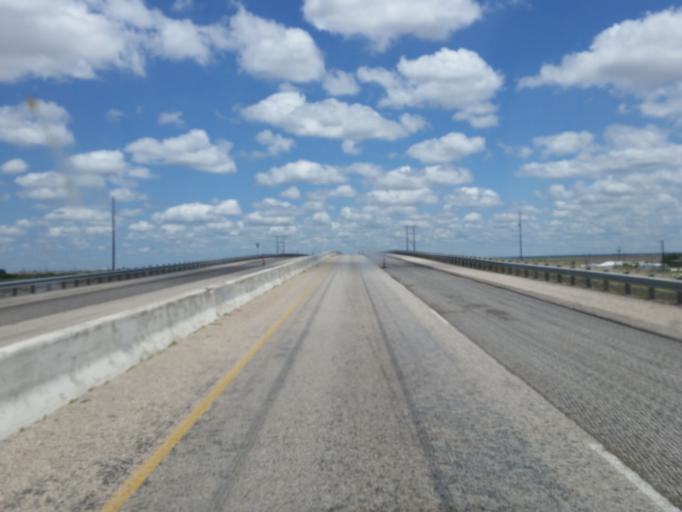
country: US
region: Texas
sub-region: Nolan County
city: Roscoe
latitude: 32.4512
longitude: -100.5232
